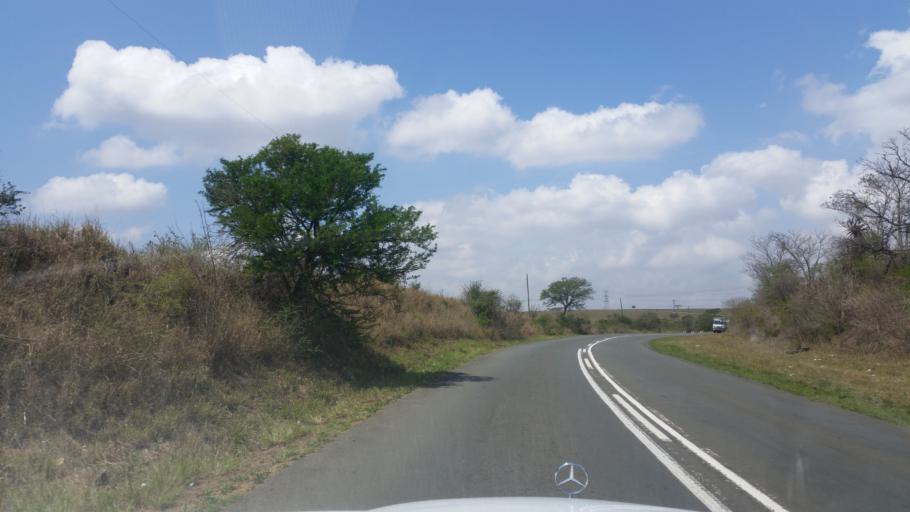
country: ZA
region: KwaZulu-Natal
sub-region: uMgungundlovu District Municipality
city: Camperdown
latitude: -29.6910
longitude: 30.4849
